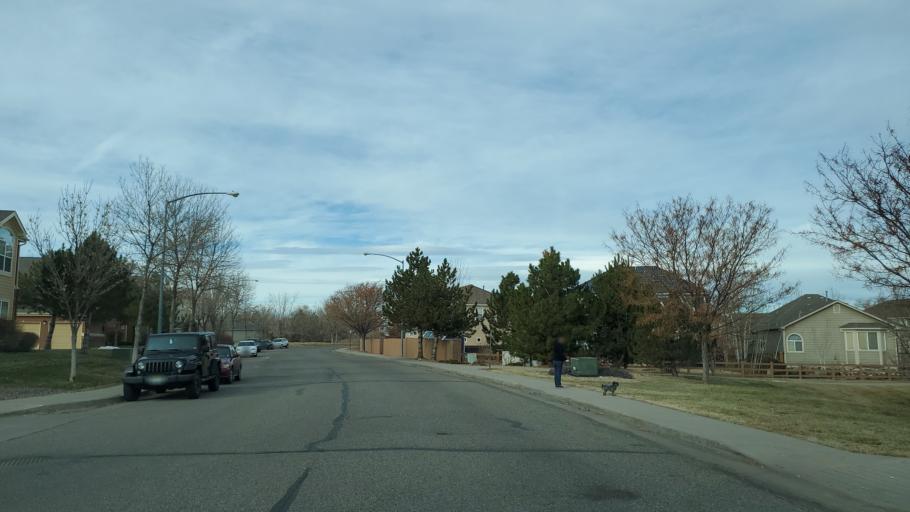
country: US
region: Colorado
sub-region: Adams County
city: Northglenn
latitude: 39.9161
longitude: -104.9480
